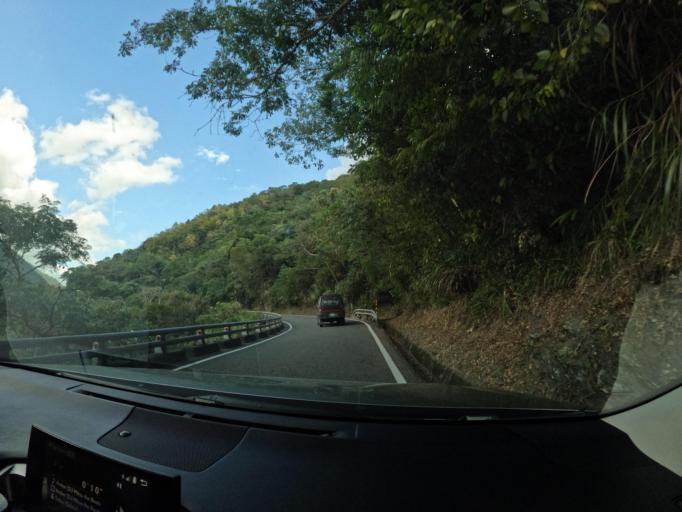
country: TW
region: Taiwan
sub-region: Taitung
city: Taitung
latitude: 23.1641
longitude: 121.0476
